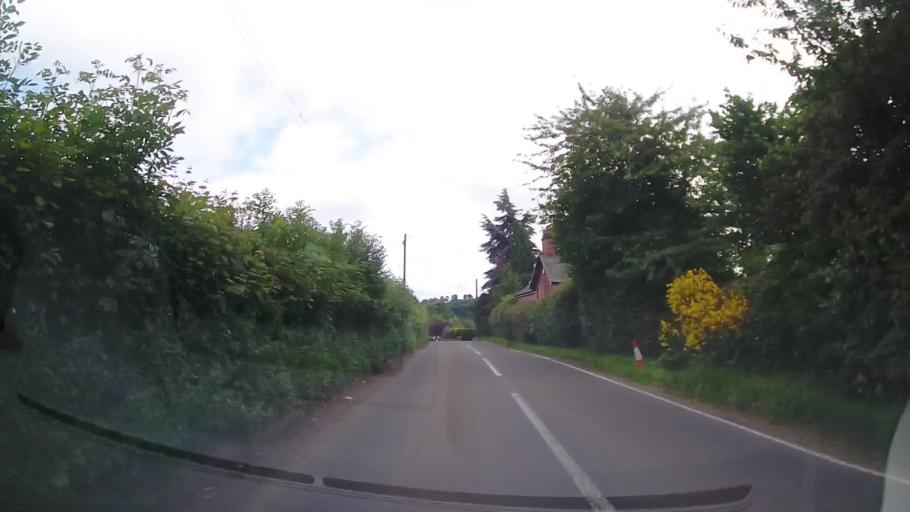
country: GB
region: Wales
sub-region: Sir Powys
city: Llanfechain
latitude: 52.8060
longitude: -3.1389
